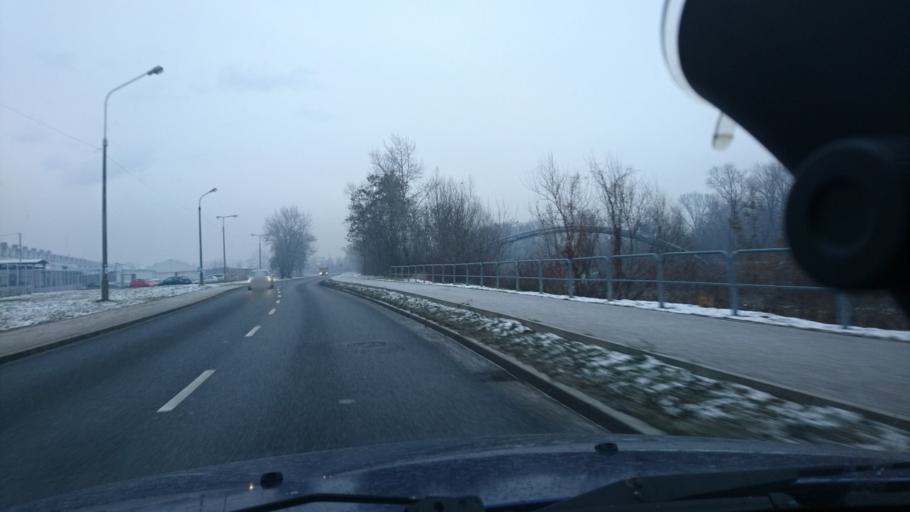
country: PL
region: Silesian Voivodeship
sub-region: Bielsko-Biala
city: Bielsko-Biala
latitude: 49.8433
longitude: 19.0469
